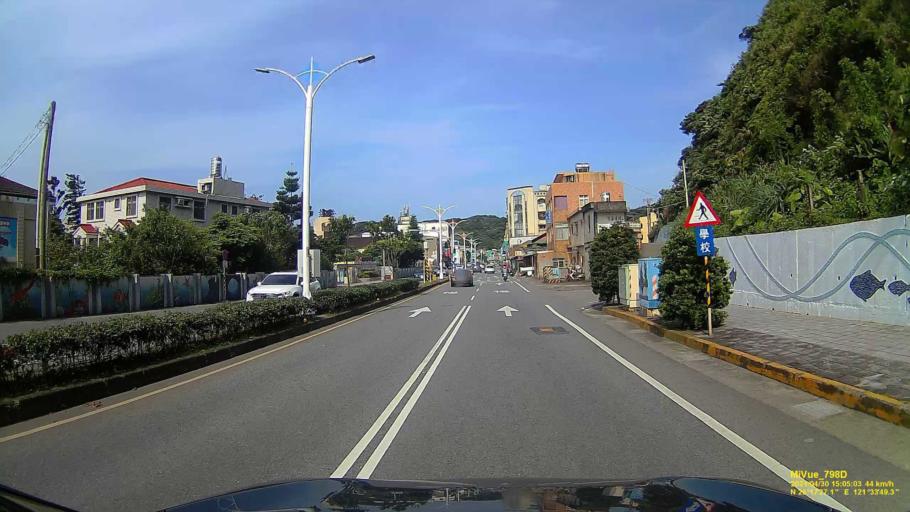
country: TW
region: Taiwan
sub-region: Keelung
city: Keelung
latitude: 25.2909
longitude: 121.5640
